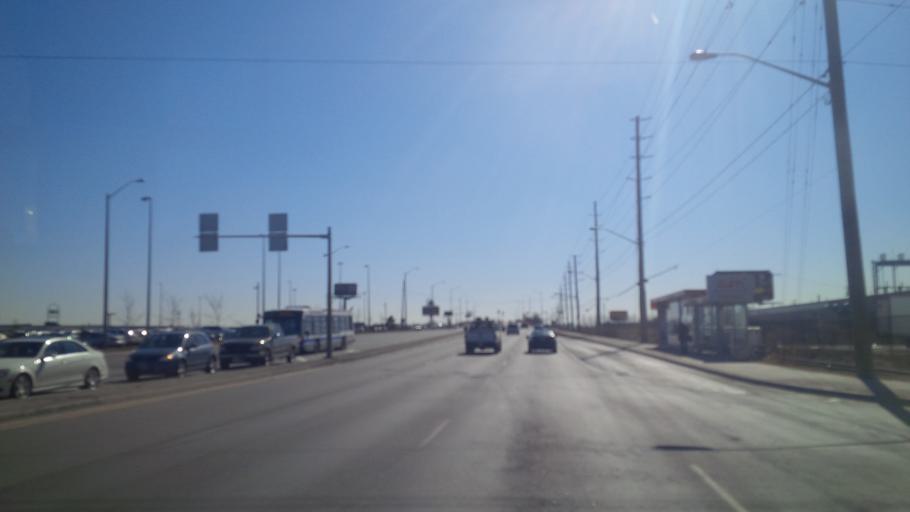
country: CA
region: Ontario
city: Brampton
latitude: 43.7048
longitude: -79.6907
